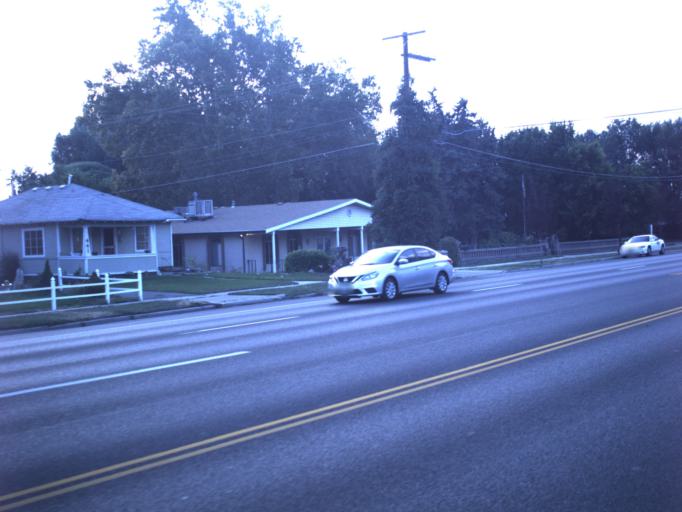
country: US
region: Utah
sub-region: Utah County
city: Springville
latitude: 40.1726
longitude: -111.6105
